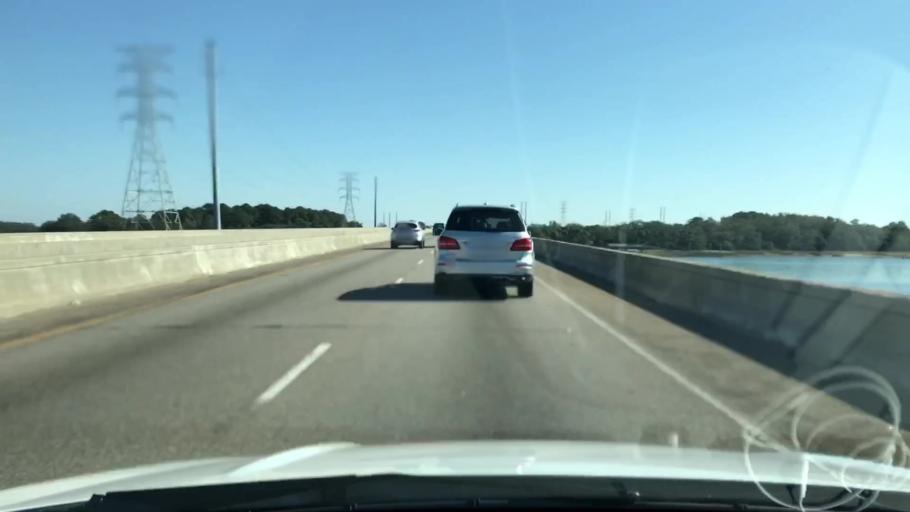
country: US
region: South Carolina
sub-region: Beaufort County
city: Hilton Head Island
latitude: 32.2305
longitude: -80.7921
